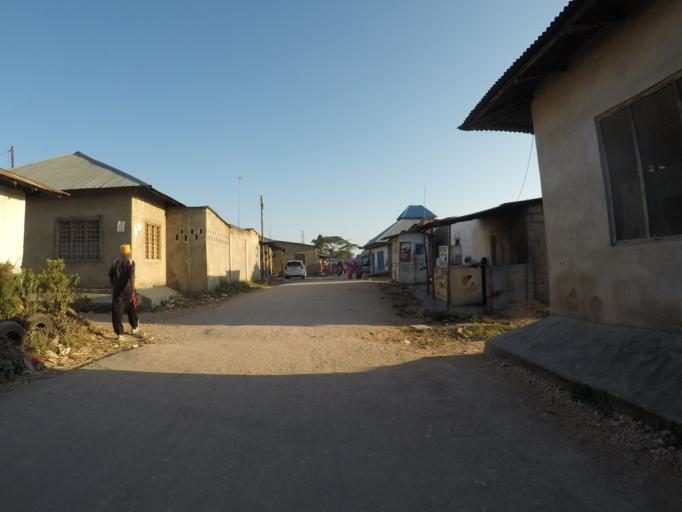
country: TZ
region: Zanzibar Urban/West
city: Zanzibar
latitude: -6.1616
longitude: 39.2178
